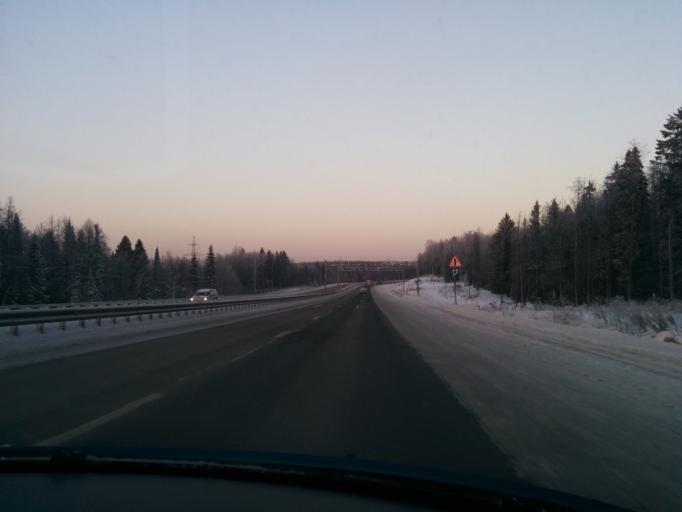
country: RU
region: Perm
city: Ferma
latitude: 58.0084
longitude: 56.3976
